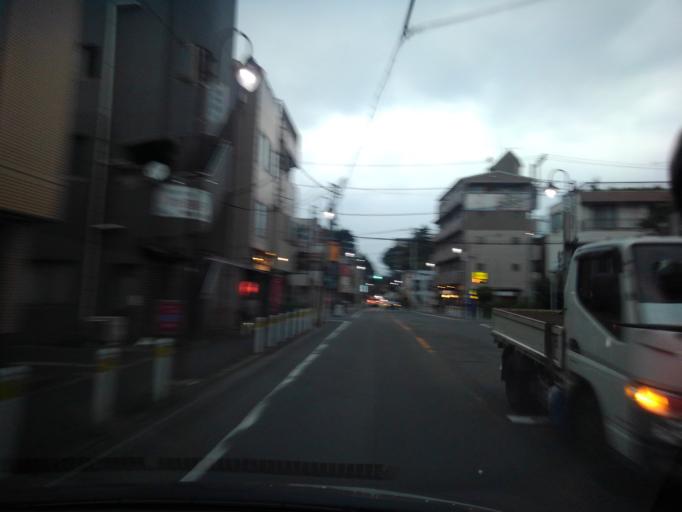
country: JP
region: Tokyo
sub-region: Machida-shi
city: Machida
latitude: 35.5721
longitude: 139.3928
